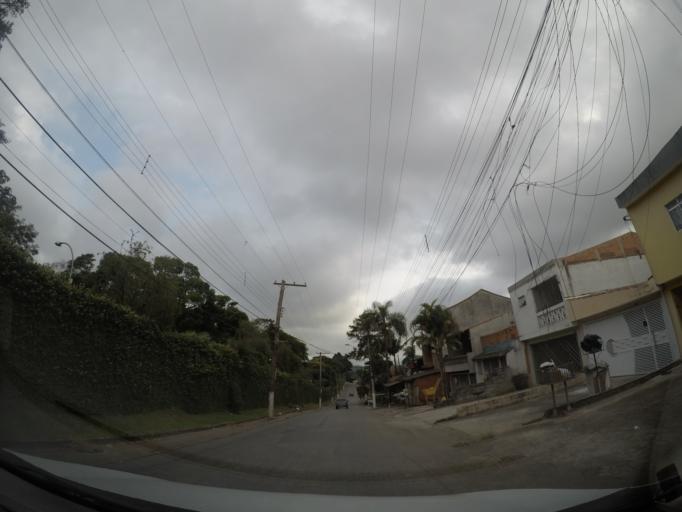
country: BR
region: Sao Paulo
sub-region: Aruja
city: Aruja
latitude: -23.4094
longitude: -46.3743
